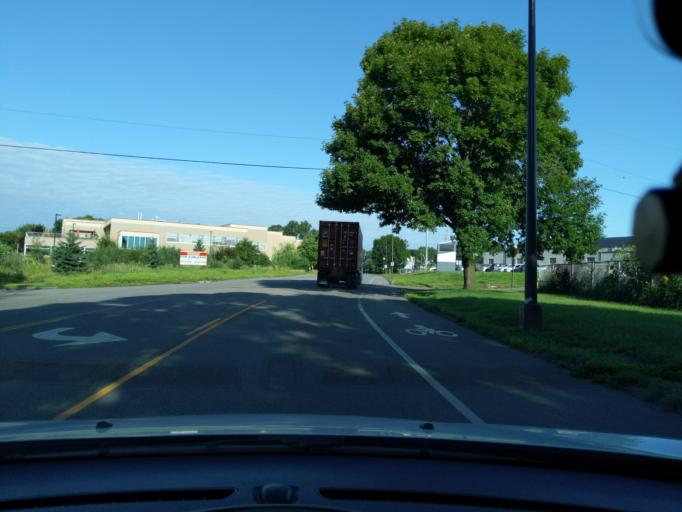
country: US
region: Minnesota
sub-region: Ramsey County
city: Falcon Heights
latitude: 44.9650
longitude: -93.1387
